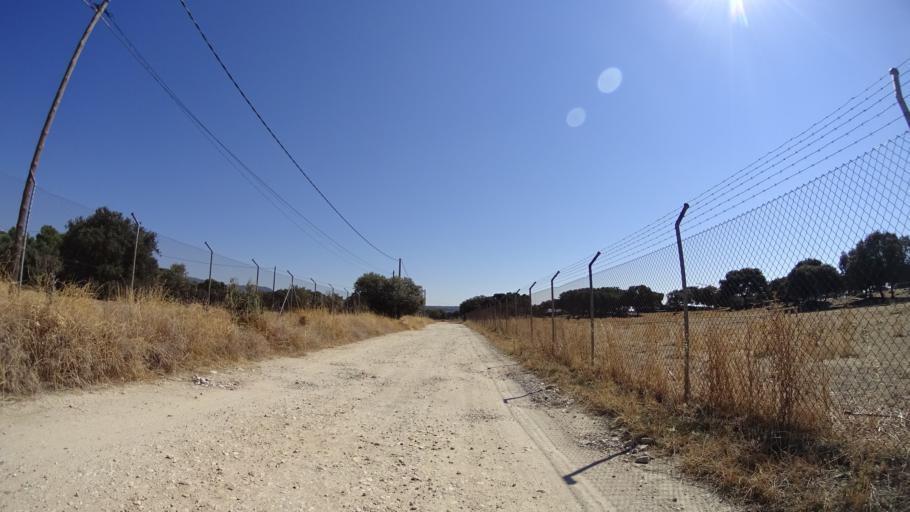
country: ES
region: Madrid
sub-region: Provincia de Madrid
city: Collado-Villalba
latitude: 40.6154
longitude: -4.0016
